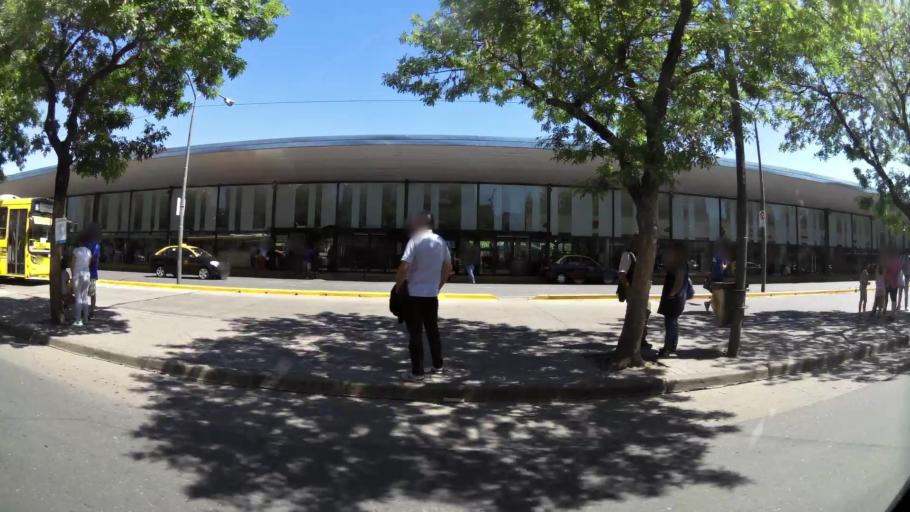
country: AR
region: Santa Fe
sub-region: Departamento de Rosario
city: Rosario
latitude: -32.9388
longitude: -60.6729
